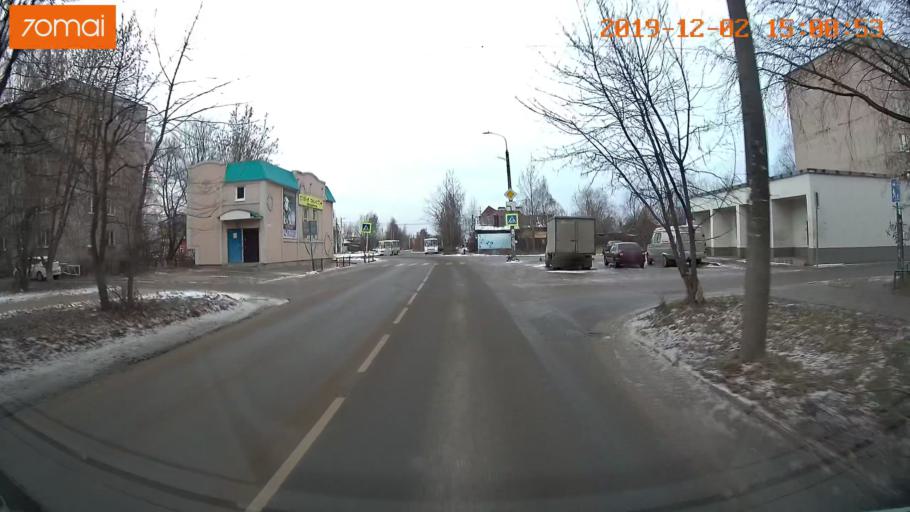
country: RU
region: Ivanovo
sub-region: Gorod Ivanovo
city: Ivanovo
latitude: 56.9728
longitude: 41.0013
